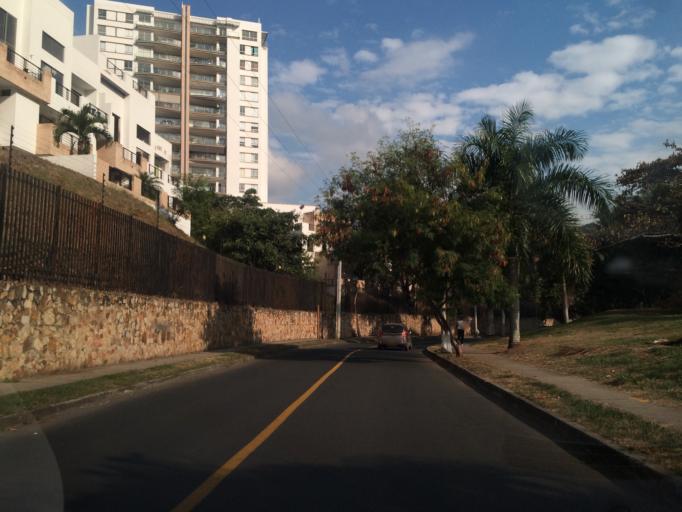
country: CO
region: Valle del Cauca
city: Cali
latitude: 3.4572
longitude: -76.5511
